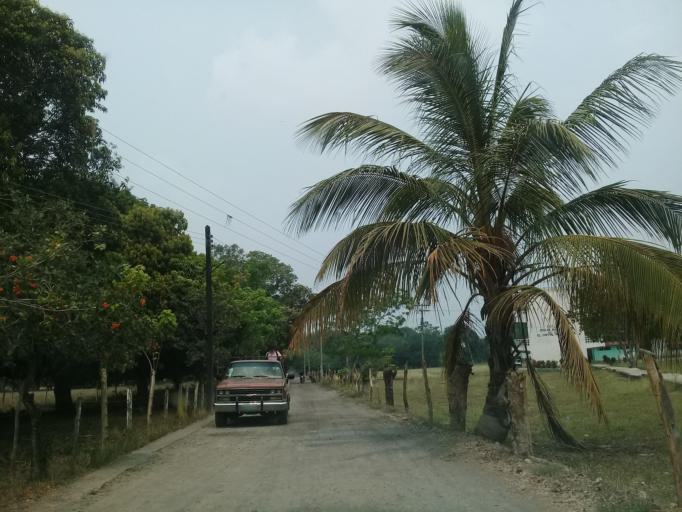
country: MX
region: Veracruz
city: Jamapa
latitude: 18.9521
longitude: -96.1975
